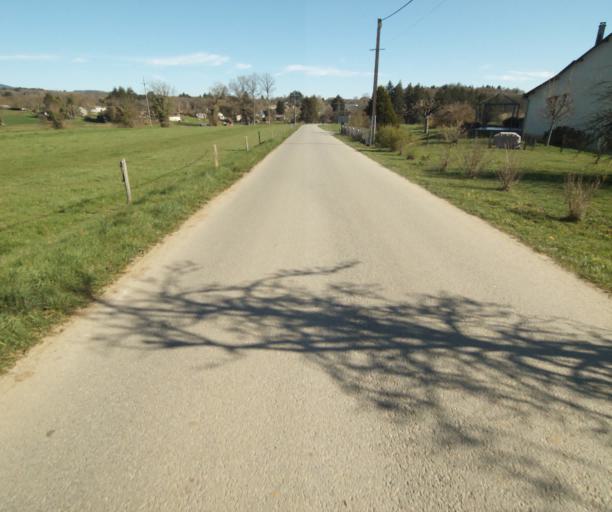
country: FR
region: Limousin
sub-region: Departement de la Correze
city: Chamboulive
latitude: 45.4730
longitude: 1.7194
